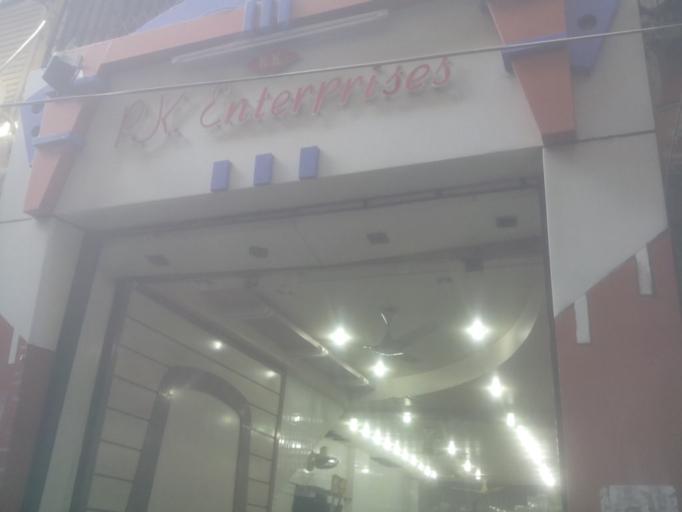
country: IN
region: Maharashtra
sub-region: Thane
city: Ulhasnagar
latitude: 19.2344
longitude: 73.1623
